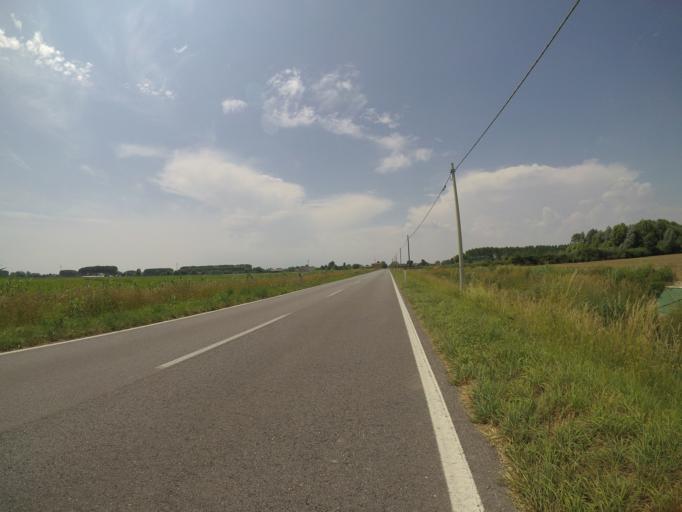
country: IT
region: Friuli Venezia Giulia
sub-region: Provincia di Udine
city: Teor
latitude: 45.8705
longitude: 13.0749
